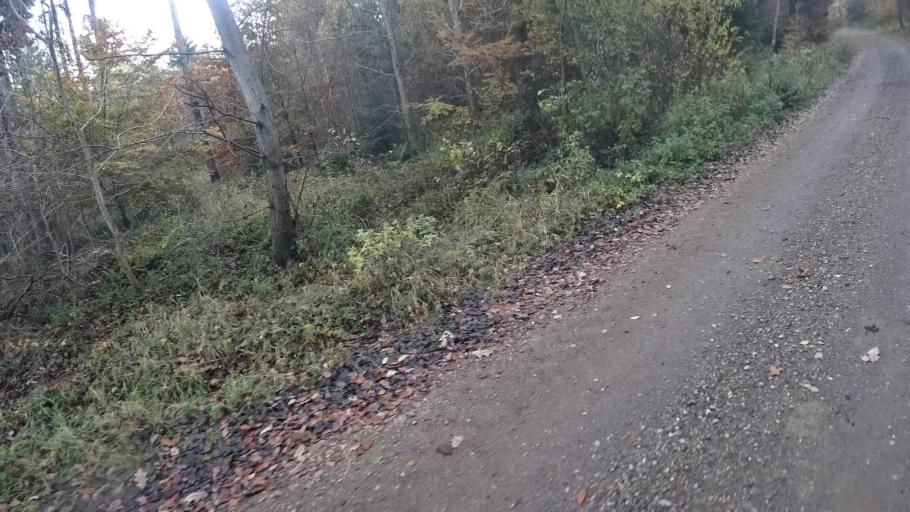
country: DE
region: Rheinland-Pfalz
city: Bickenbach
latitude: 50.1130
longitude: 7.5357
